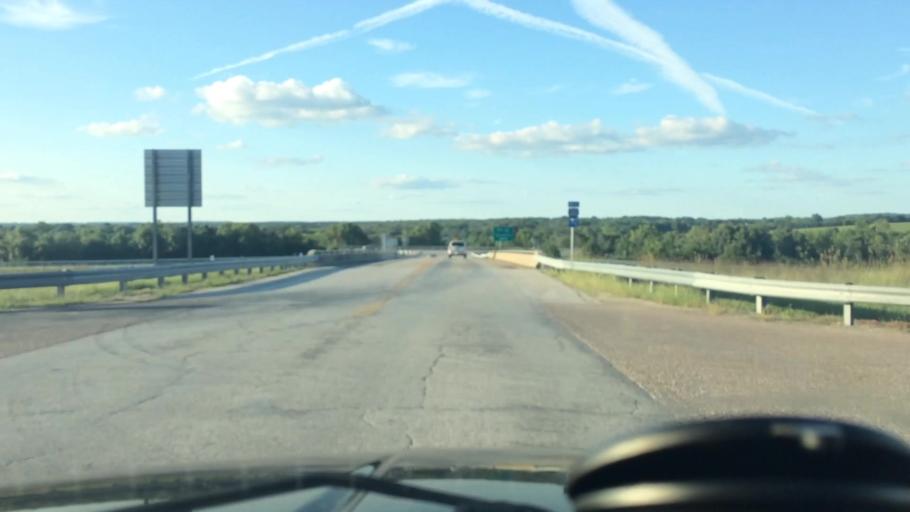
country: US
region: Missouri
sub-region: Webster County
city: Marshfield
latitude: 37.3008
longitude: -92.9995
